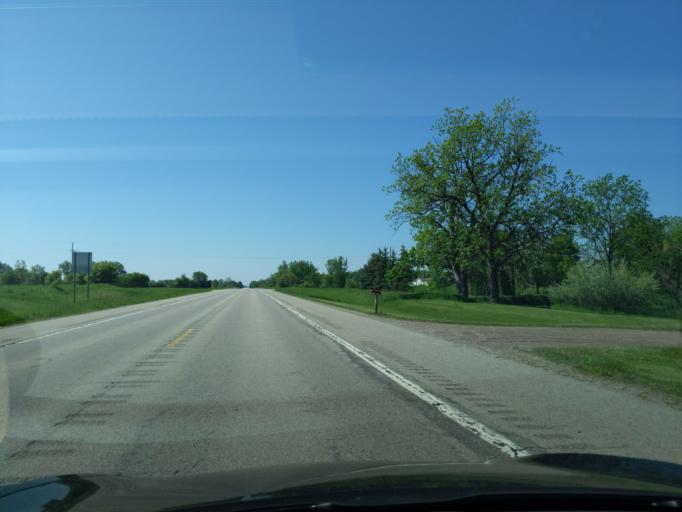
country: US
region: Michigan
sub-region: Ingham County
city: Stockbridge
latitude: 42.5419
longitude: -84.1913
